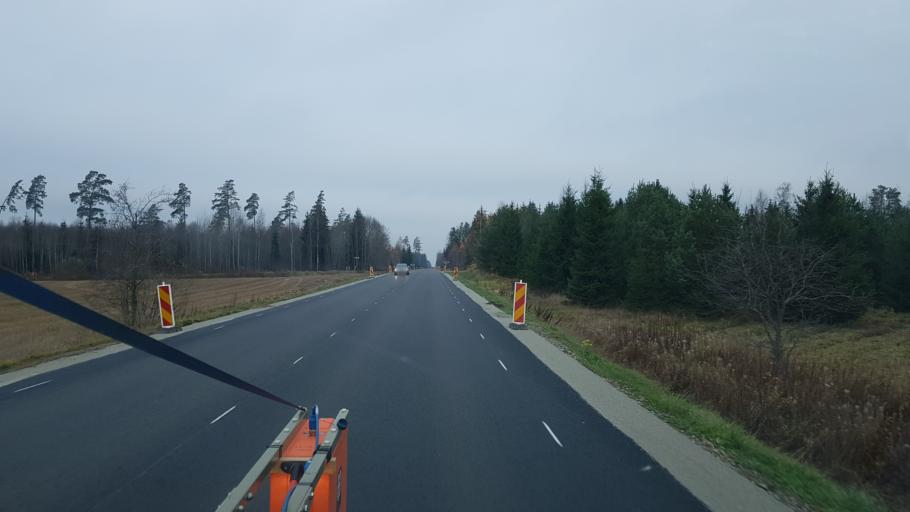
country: EE
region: Paernumaa
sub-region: Vaendra vald (alev)
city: Vandra
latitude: 58.8248
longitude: 25.1260
